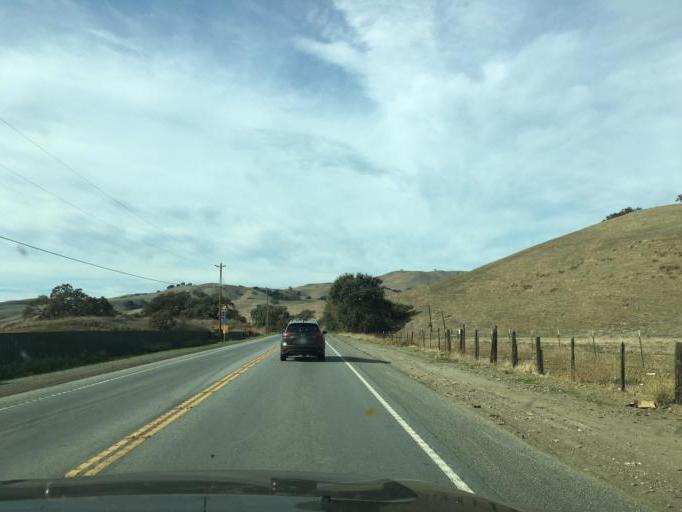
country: US
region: California
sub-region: Santa Clara County
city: Gilroy
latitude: 36.9864
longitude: -121.4444
